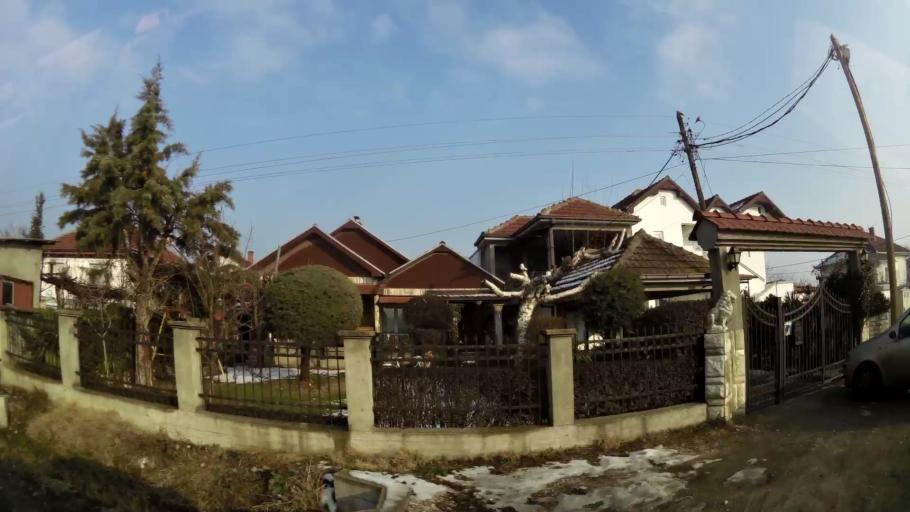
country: MK
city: Kadino
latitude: 41.9683
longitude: 21.5965
